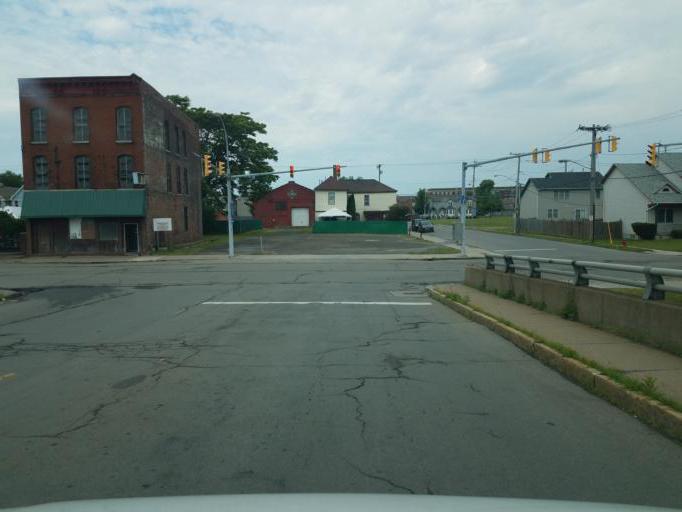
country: US
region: New York
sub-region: Erie County
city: Buffalo
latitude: 42.8779
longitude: -78.8626
